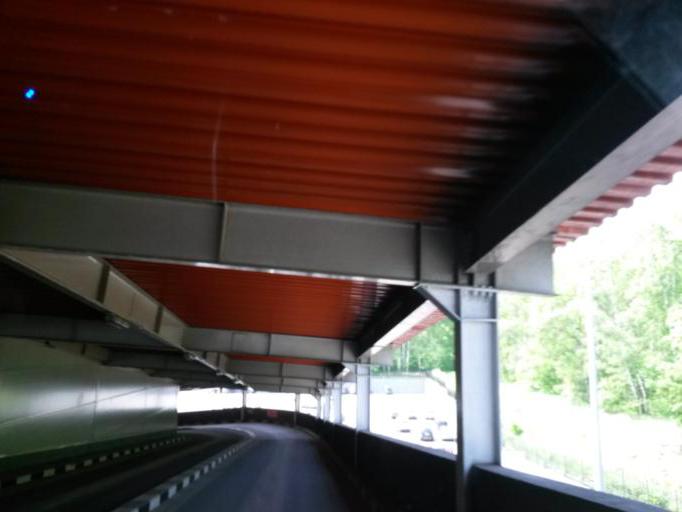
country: RU
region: Moscow
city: Chertanovo Yuzhnoye
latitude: 55.5660
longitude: 37.5563
